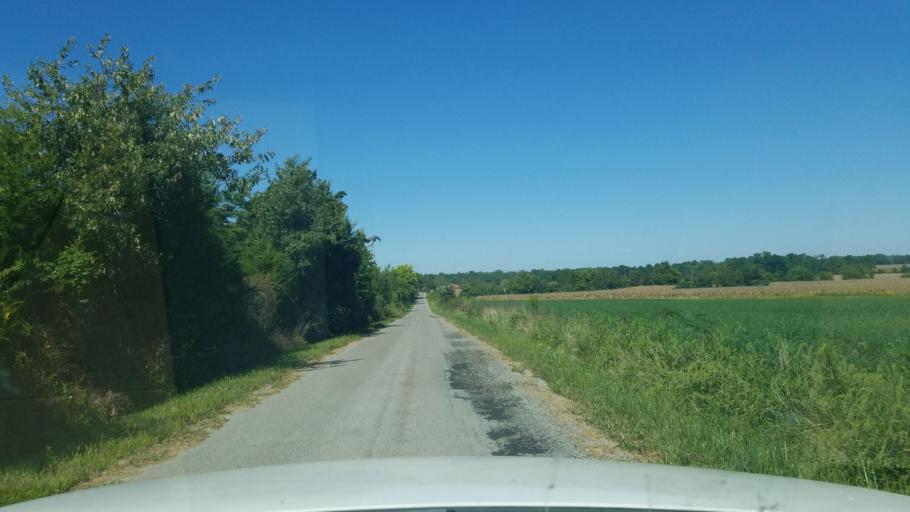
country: US
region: Illinois
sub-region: Saline County
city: Eldorado
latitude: 37.8567
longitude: -88.5119
